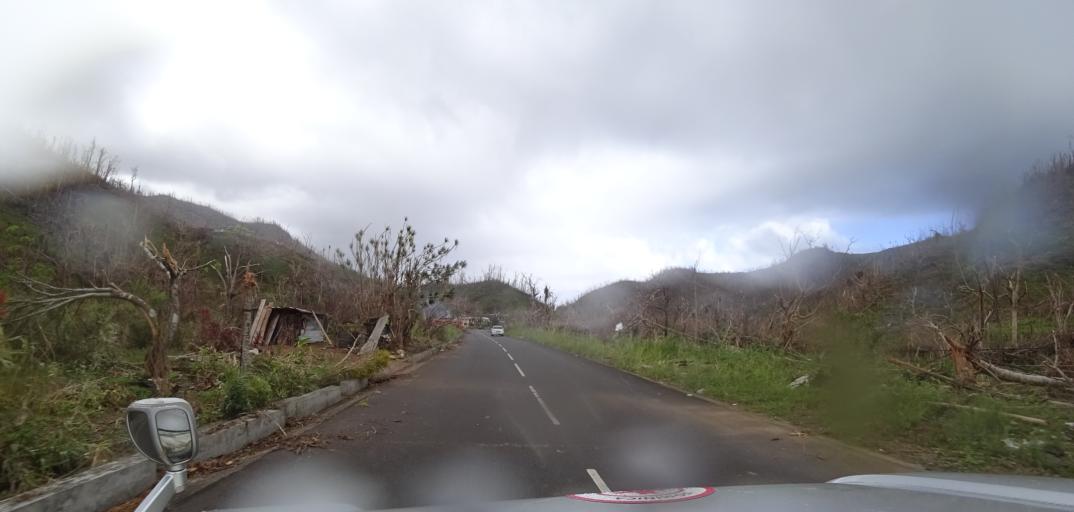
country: DM
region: Saint Andrew
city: Marigot
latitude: 15.4966
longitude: -61.2771
